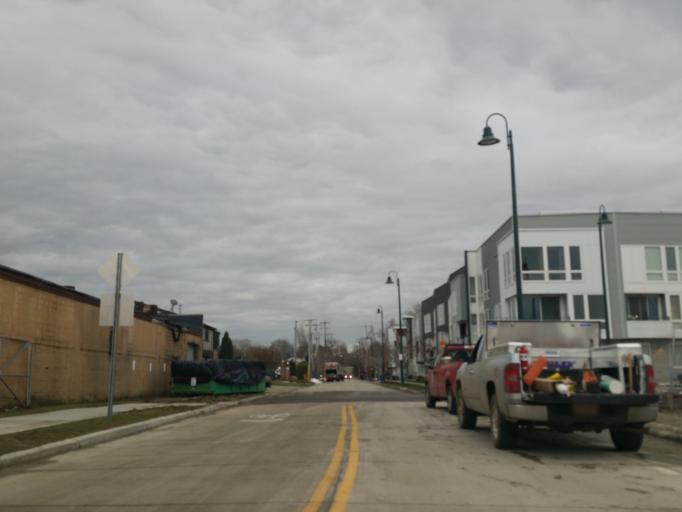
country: US
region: Ohio
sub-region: Cuyahoga County
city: Cleveland
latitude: 41.4872
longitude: -81.7347
